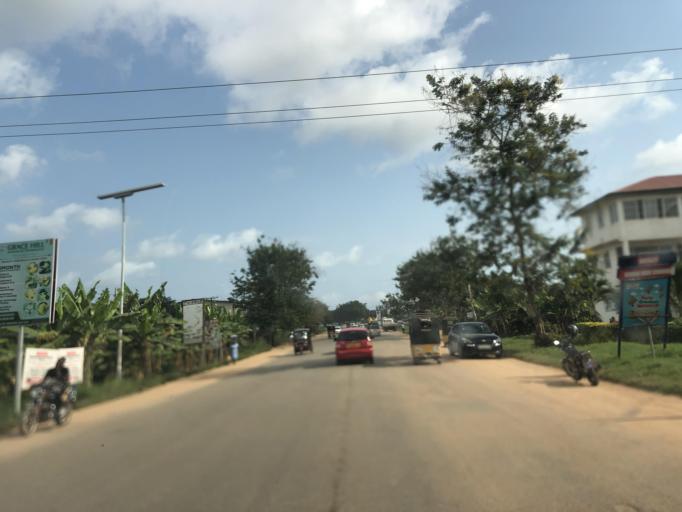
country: GH
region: Central
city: Cape Coast
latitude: 5.1401
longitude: -1.2819
